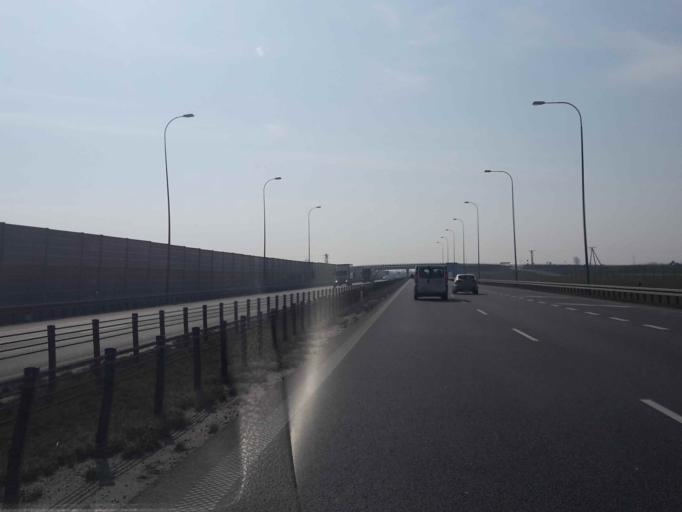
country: PL
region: Kujawsko-Pomorskie
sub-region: Powiat torunski
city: Lubicz Dolny
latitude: 53.0851
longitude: 18.7509
